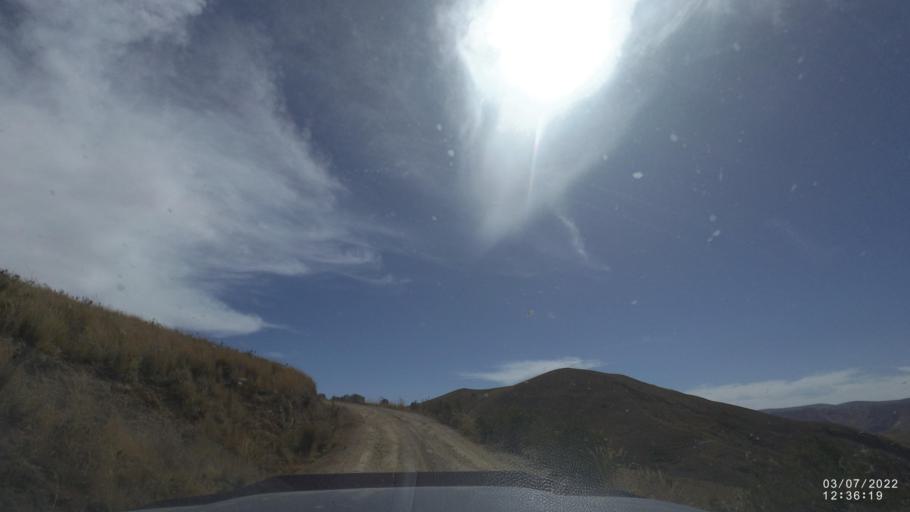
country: BO
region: Cochabamba
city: Irpa Irpa
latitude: -17.8022
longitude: -66.6121
